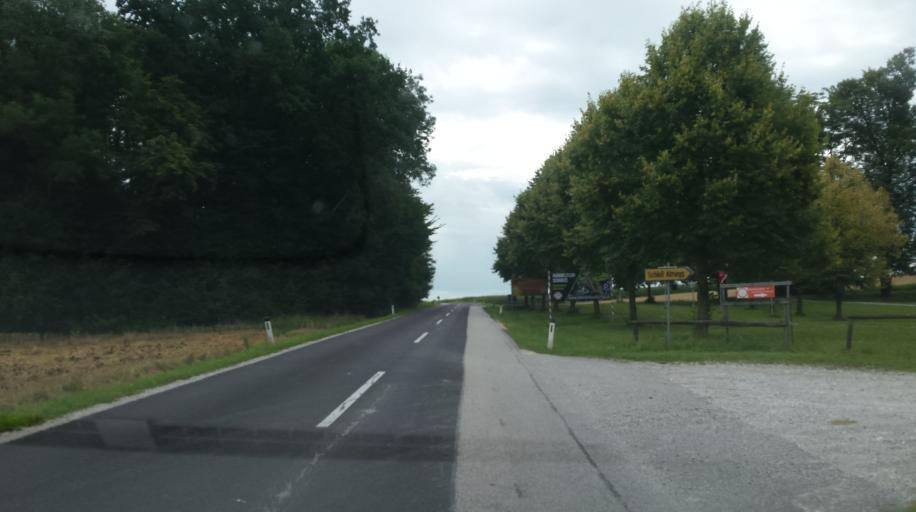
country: AT
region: Upper Austria
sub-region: Wels-Land
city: Bad Wimsbach-Neydharting
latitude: 48.0717
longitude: 13.9231
